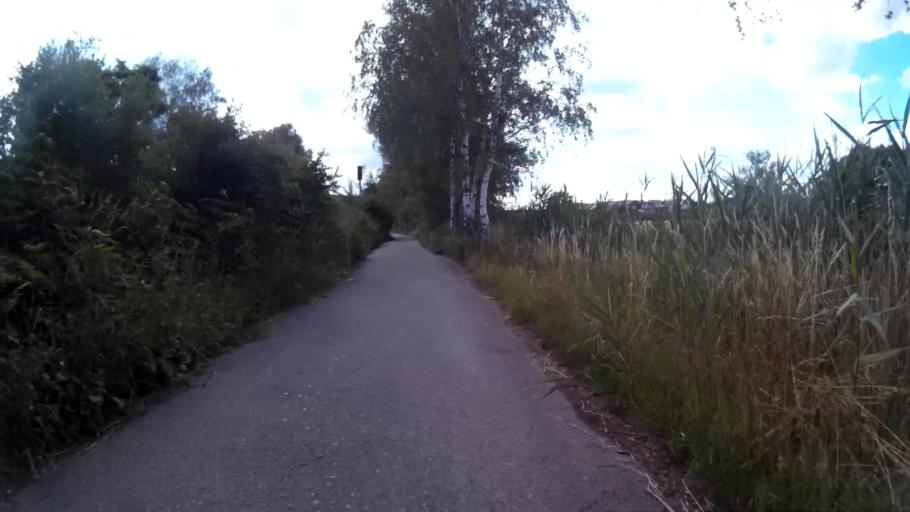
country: CZ
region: South Moravian
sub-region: Okres Brno-Venkov
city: Rosice
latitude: 49.1744
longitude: 16.4005
